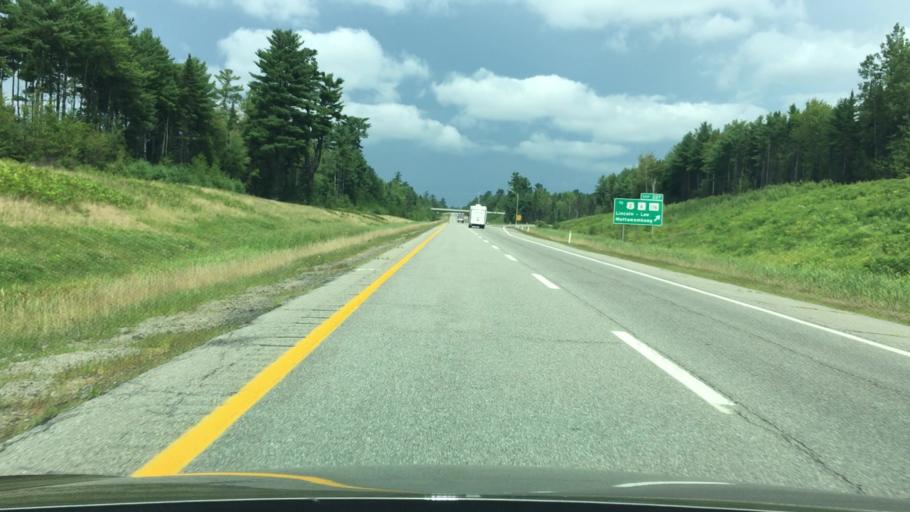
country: US
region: Maine
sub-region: Penobscot County
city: Lincoln
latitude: 45.3702
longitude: -68.6049
